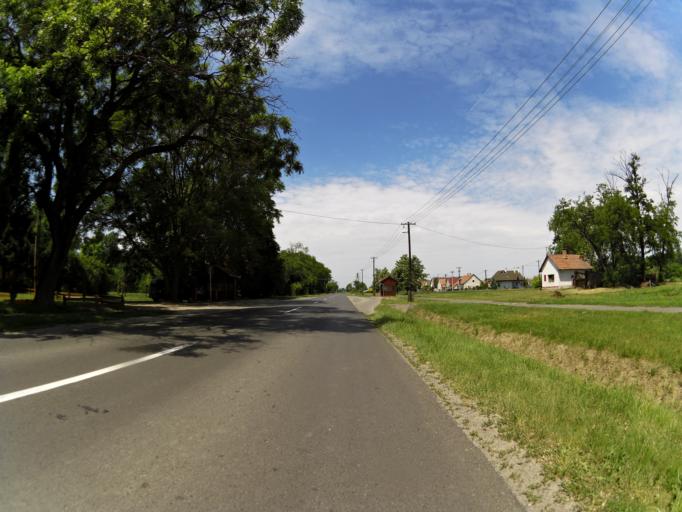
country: HU
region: Csongrad
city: Opusztaszer
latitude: 46.4894
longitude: 20.0735
